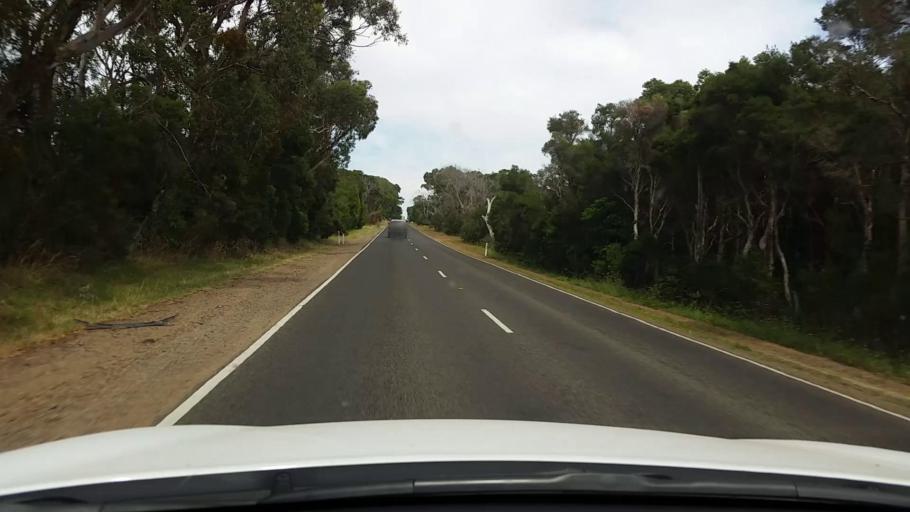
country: AU
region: Victoria
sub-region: Mornington Peninsula
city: Merricks
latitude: -38.3853
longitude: 145.1016
